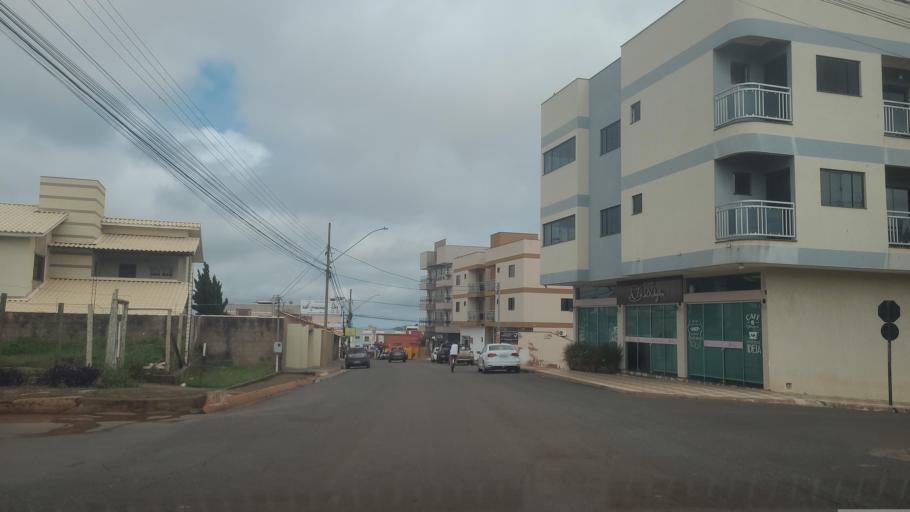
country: BR
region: Minas Gerais
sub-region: Carmo Do Paranaiba
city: Carmo do Paranaiba
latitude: -19.1970
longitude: -46.2378
